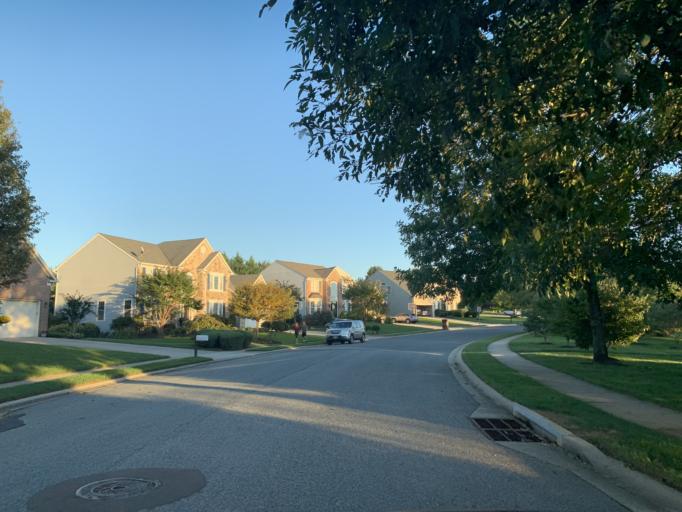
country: US
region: Maryland
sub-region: Harford County
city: Bel Air South
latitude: 39.5288
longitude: -76.2973
